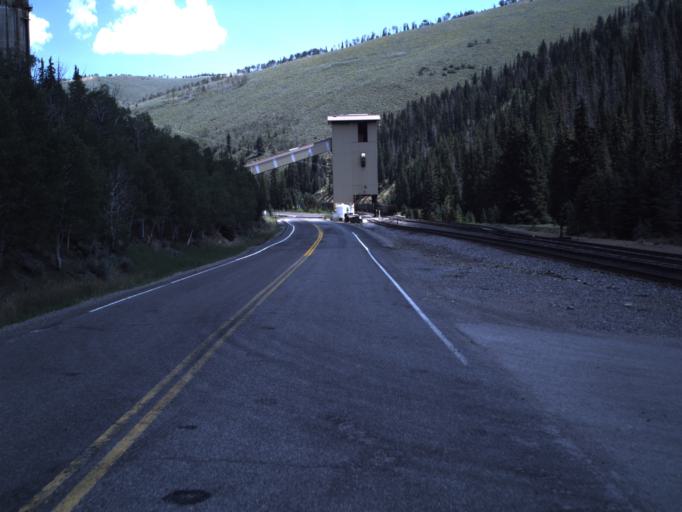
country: US
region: Utah
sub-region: Sanpete County
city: Fairview
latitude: 39.6821
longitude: -111.1587
